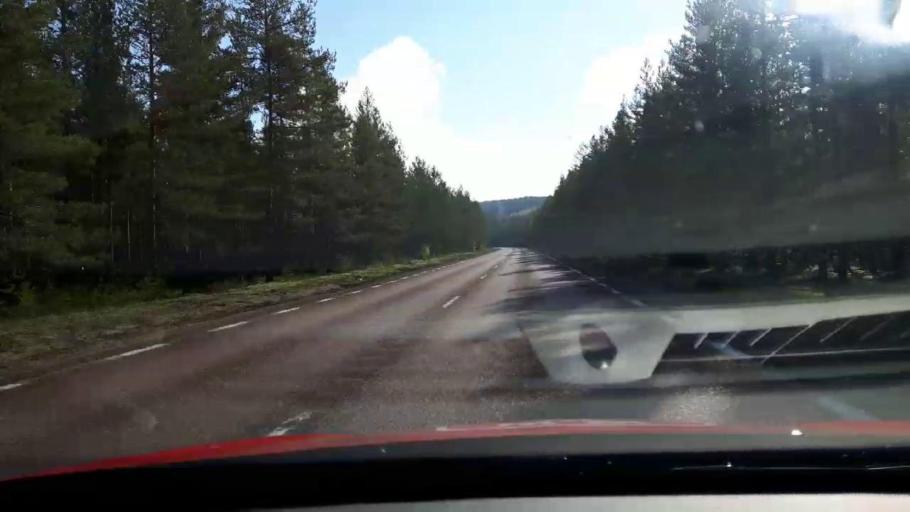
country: SE
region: Gaevleborg
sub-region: Ljusdals Kommun
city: Farila
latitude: 61.8920
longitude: 15.6637
